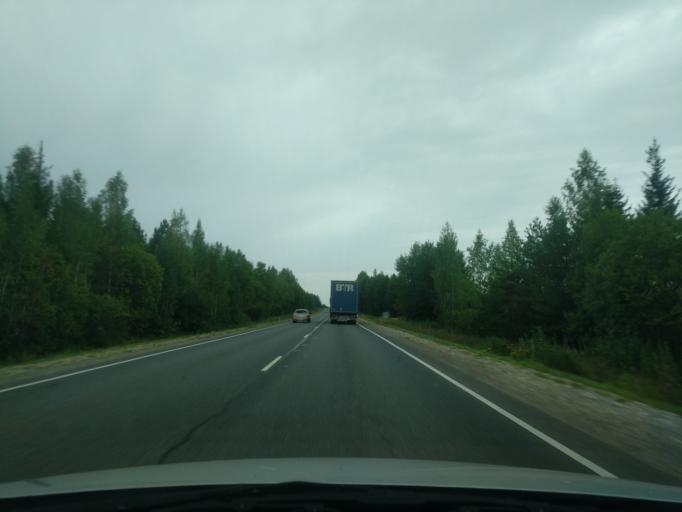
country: RU
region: Kirov
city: Kotel'nich
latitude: 58.4752
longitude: 48.5619
